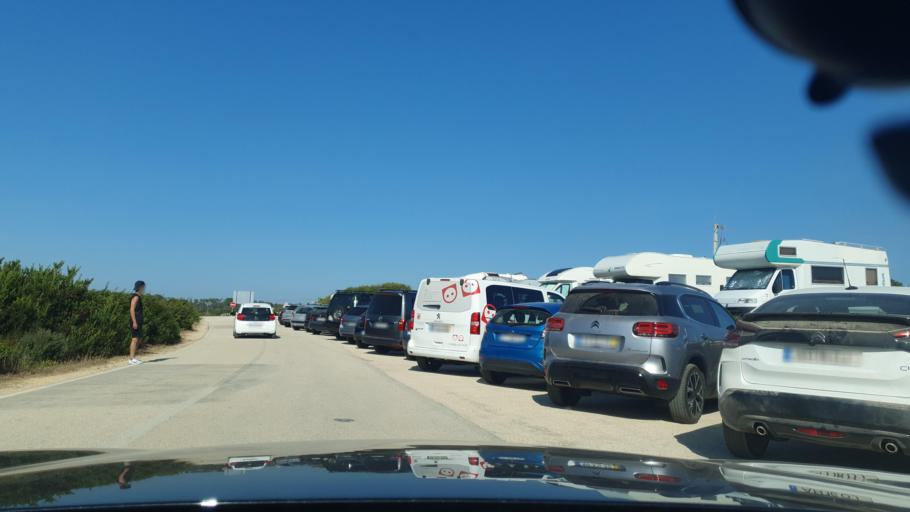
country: PT
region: Beja
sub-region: Odemira
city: Sao Teotonio
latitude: 37.4381
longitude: -8.7985
